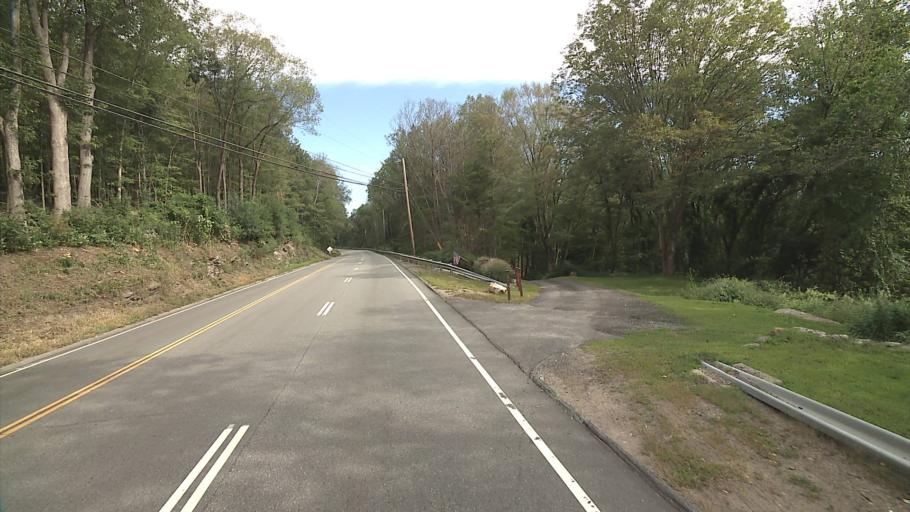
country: US
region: Connecticut
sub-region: New London County
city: Baltic
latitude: 41.6119
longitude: -72.1450
